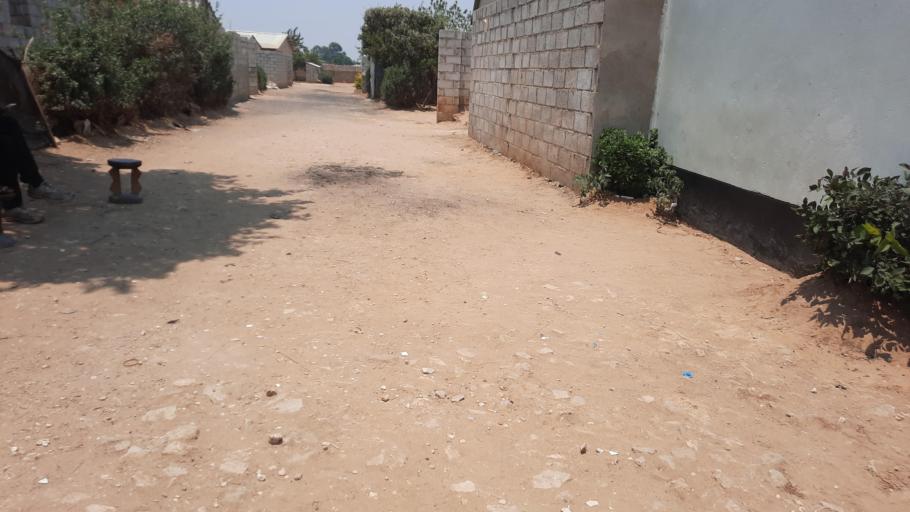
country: ZM
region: Lusaka
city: Lusaka
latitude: -15.4033
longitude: 28.3826
